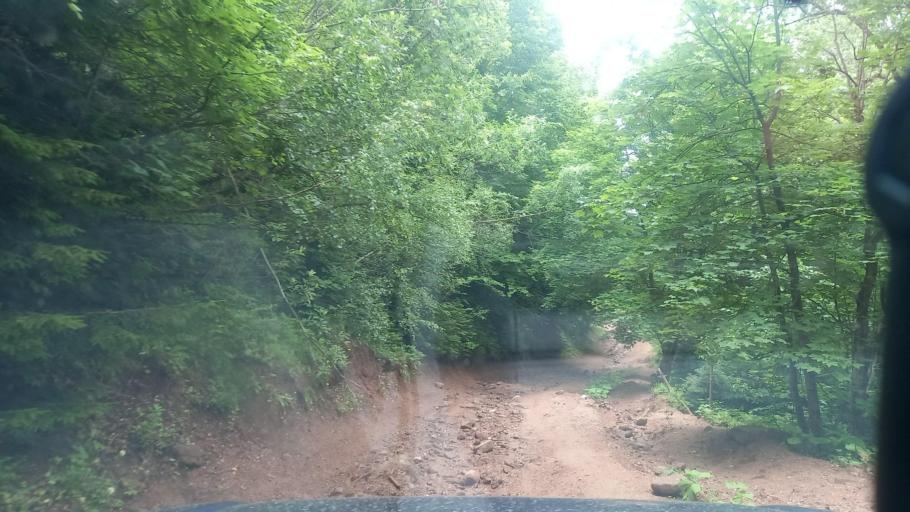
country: RU
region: Karachayevo-Cherkesiya
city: Kurdzhinovo
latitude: 43.8058
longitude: 40.8429
